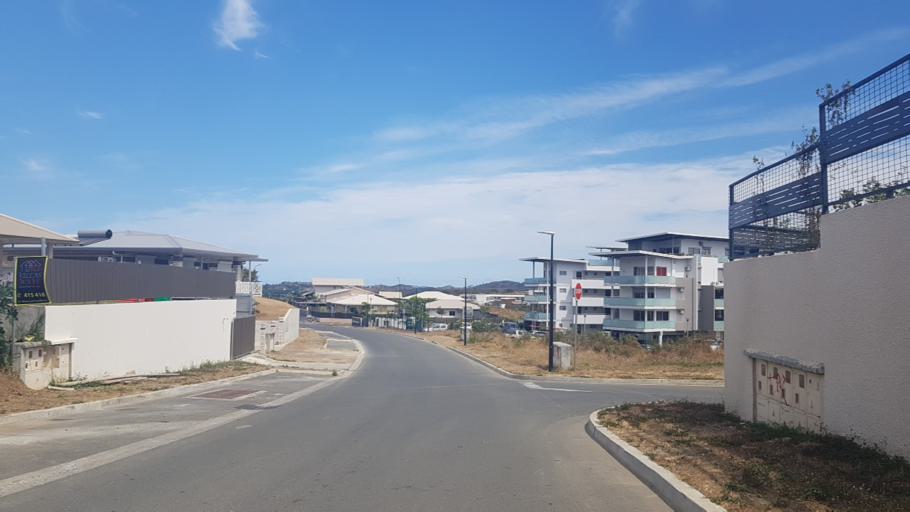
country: NC
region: South Province
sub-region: Dumbea
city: Dumbea
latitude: -22.2021
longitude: 166.4438
